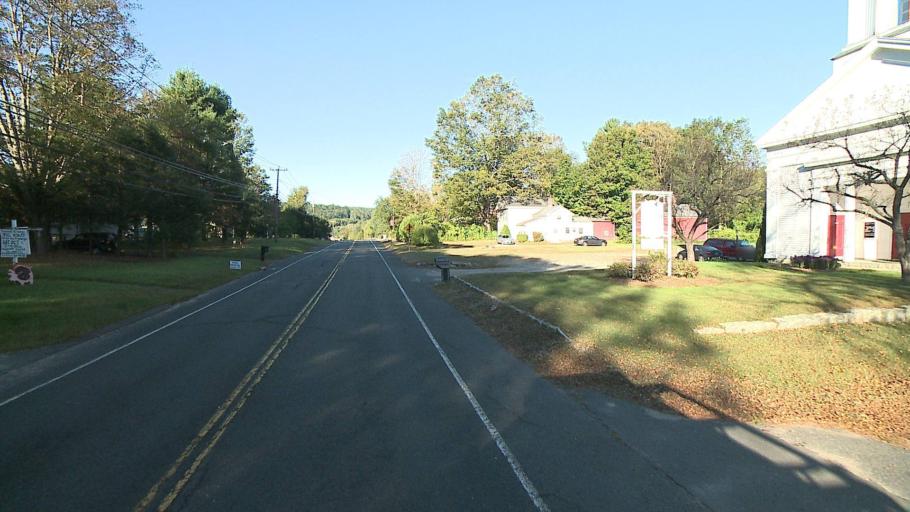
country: US
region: Connecticut
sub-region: Litchfield County
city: New Hartford Center
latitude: 41.8298
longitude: -72.9986
